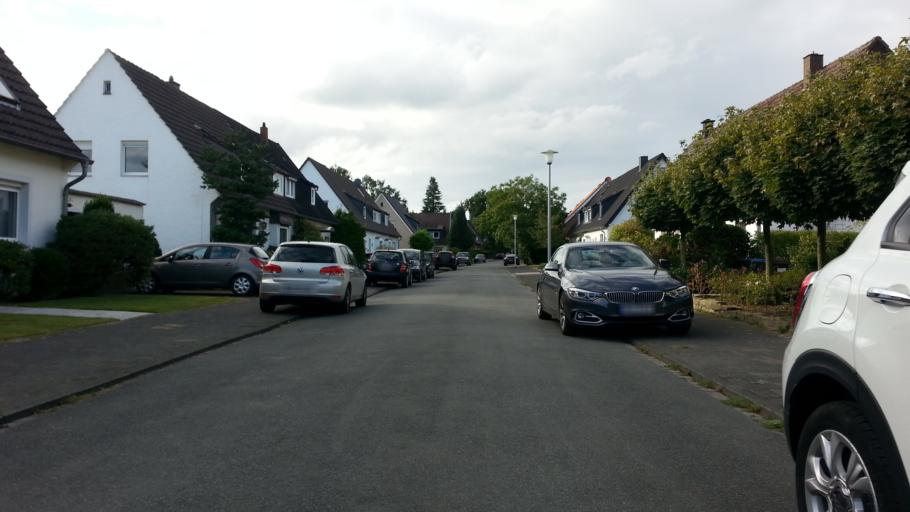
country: DE
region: North Rhine-Westphalia
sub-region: Regierungsbezirk Munster
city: Muenster
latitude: 51.9545
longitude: 7.5976
